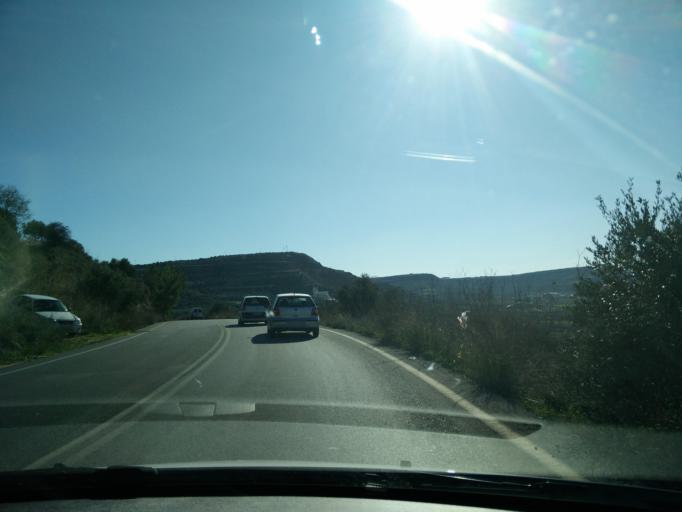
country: GR
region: Crete
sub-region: Nomos Irakleiou
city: Arkalochori
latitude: 35.1403
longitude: 25.2590
